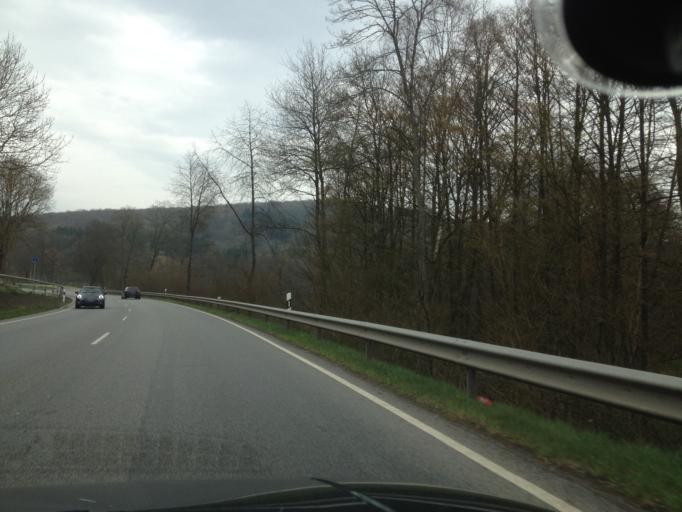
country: DE
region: Rheinland-Pfalz
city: Ruthweiler
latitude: 49.5334
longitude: 7.3789
